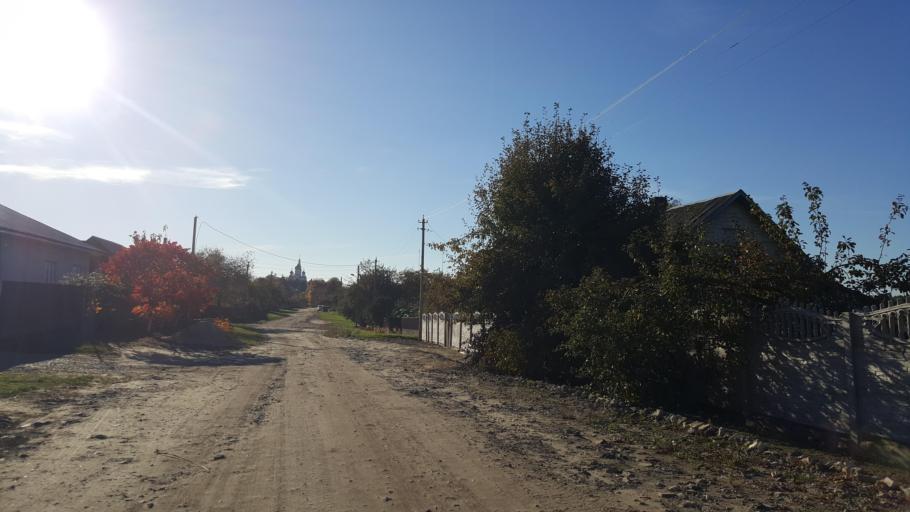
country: BY
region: Brest
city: Kamyanyets
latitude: 52.4063
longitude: 23.8341
